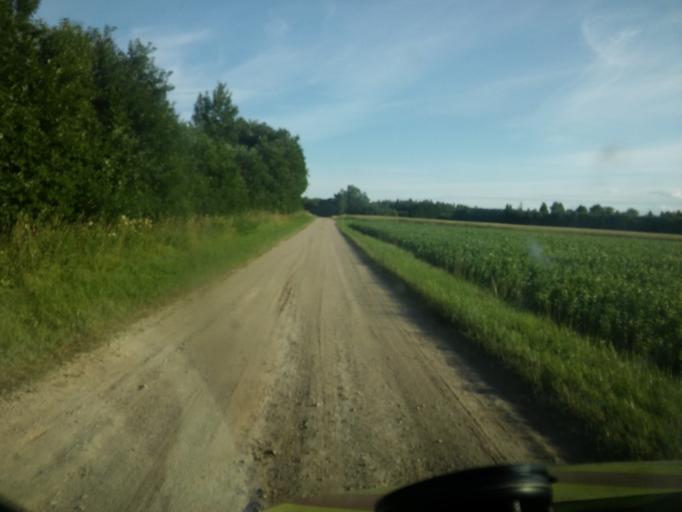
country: EE
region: Valgamaa
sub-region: Torva linn
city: Torva
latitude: 58.1005
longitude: 26.0025
